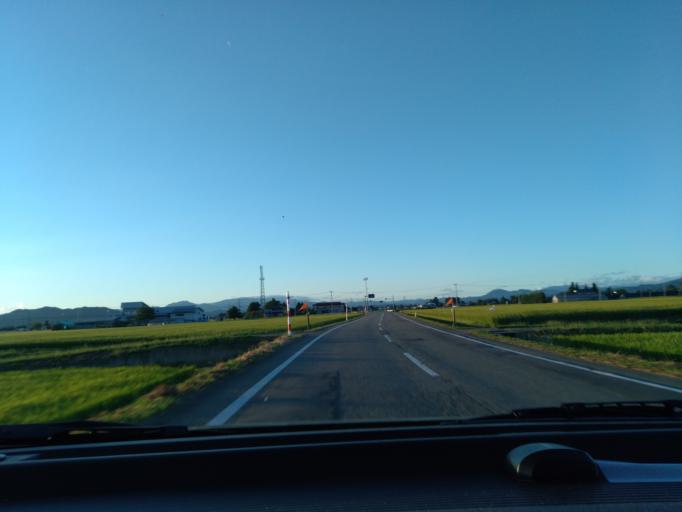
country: JP
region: Akita
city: Omagari
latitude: 39.4930
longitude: 140.5596
